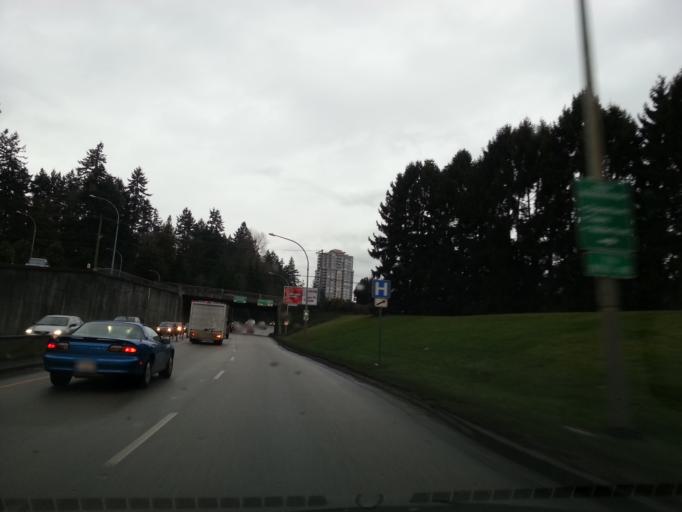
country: CA
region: British Columbia
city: New Westminster
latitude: 49.2104
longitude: -122.8995
